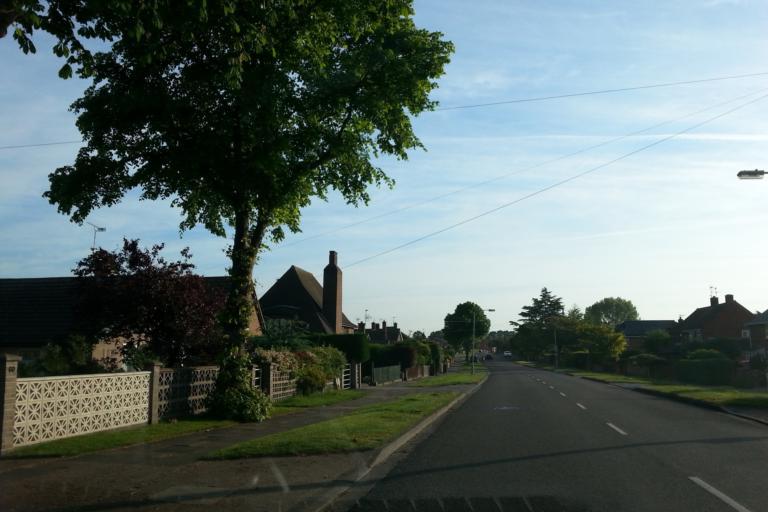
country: GB
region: England
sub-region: Nottinghamshire
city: Newark on Trent
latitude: 53.0667
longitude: -0.8182
